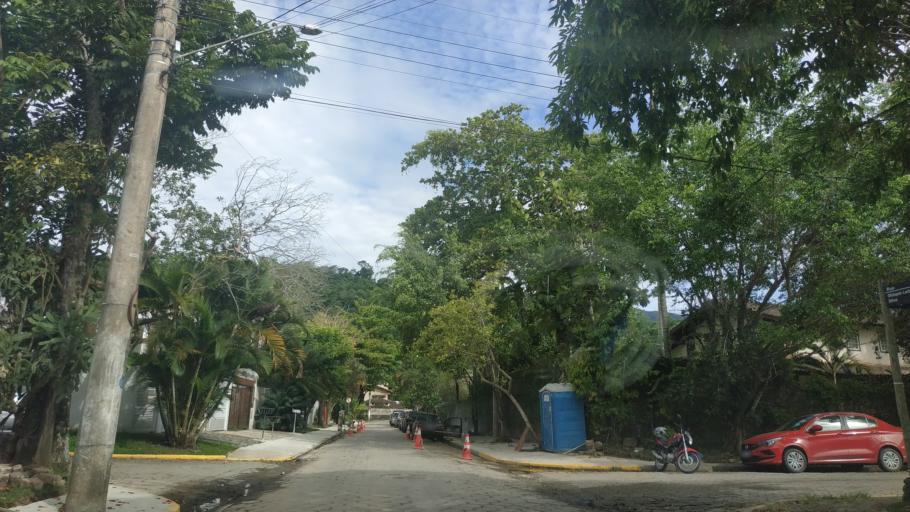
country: BR
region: Sao Paulo
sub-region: Ilhabela
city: Ilhabela
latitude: -23.8139
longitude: -45.3650
